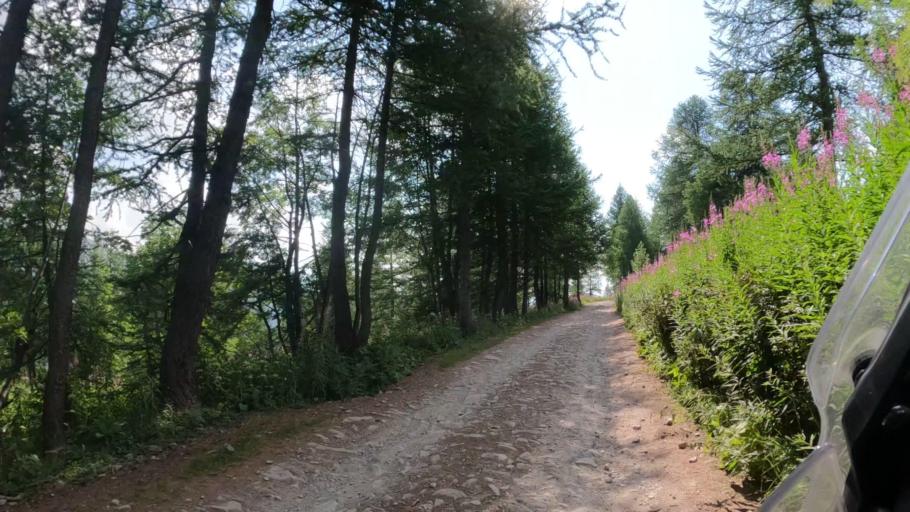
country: IT
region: Piedmont
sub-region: Provincia di Cuneo
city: Briga Alta
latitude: 44.1285
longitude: 7.6893
